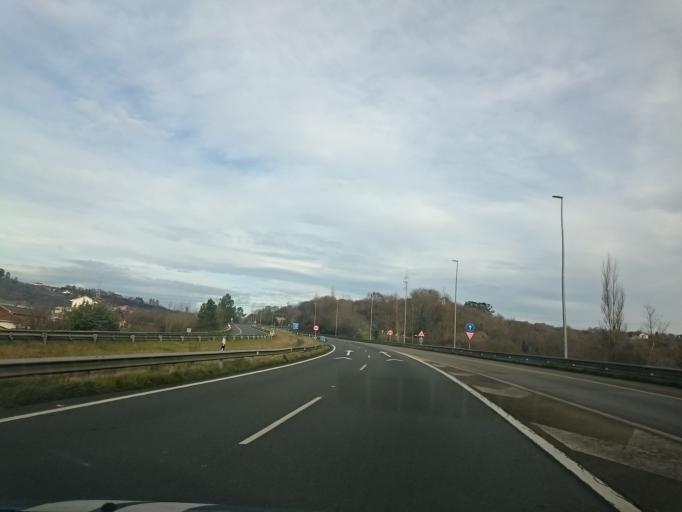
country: ES
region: Asturias
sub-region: Province of Asturias
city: Castandiello
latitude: 43.3181
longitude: -5.8689
